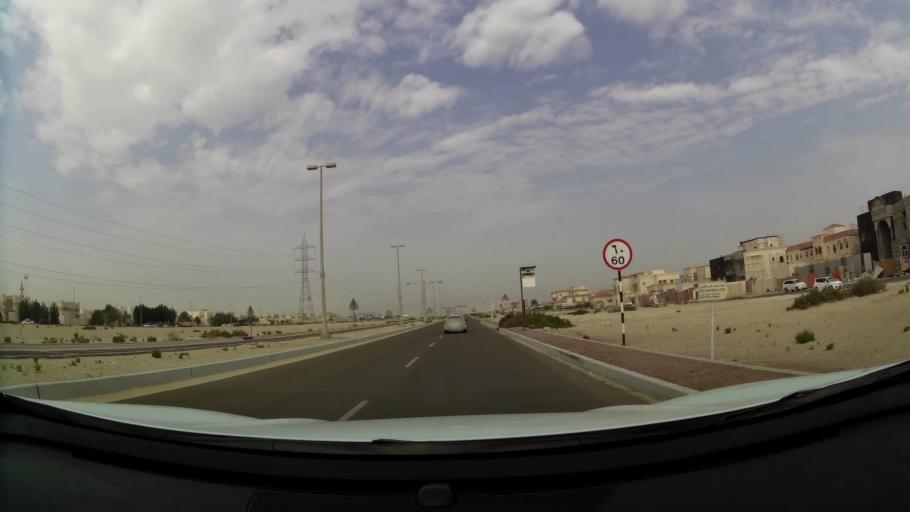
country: AE
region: Abu Dhabi
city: Abu Dhabi
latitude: 24.3081
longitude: 54.6465
